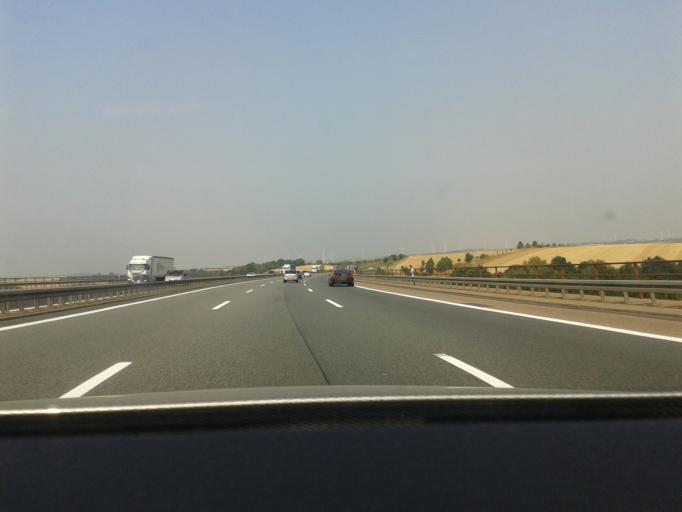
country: DE
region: Saxony
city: Reinsberg
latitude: 51.0581
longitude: 13.4304
